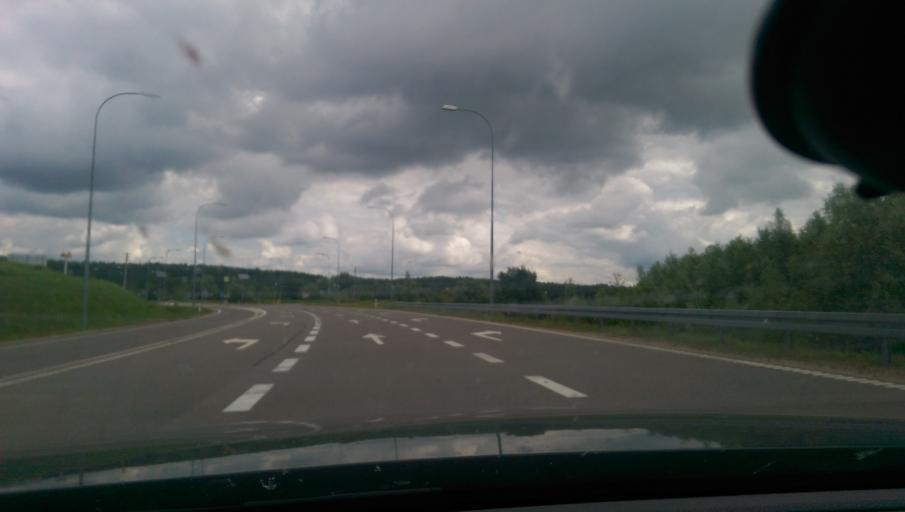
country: PL
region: Warmian-Masurian Voivodeship
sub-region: Powiat goldapski
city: Goldap
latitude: 54.3183
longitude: 22.2945
